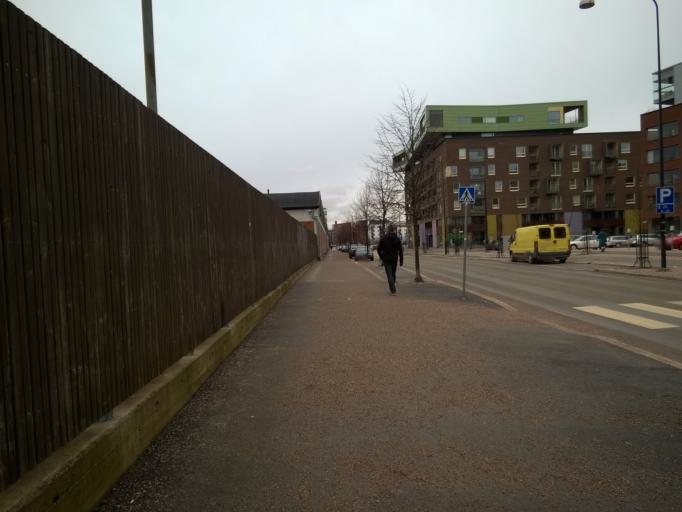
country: FI
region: Uusimaa
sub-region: Helsinki
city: Helsinki
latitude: 60.2037
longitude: 24.9709
